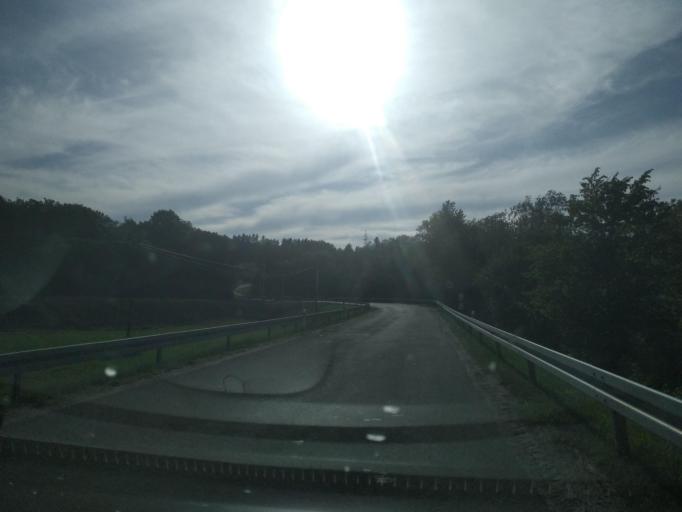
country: PL
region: Subcarpathian Voivodeship
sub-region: Powiat sanocki
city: Rzepedz
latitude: 49.4122
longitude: 22.1385
